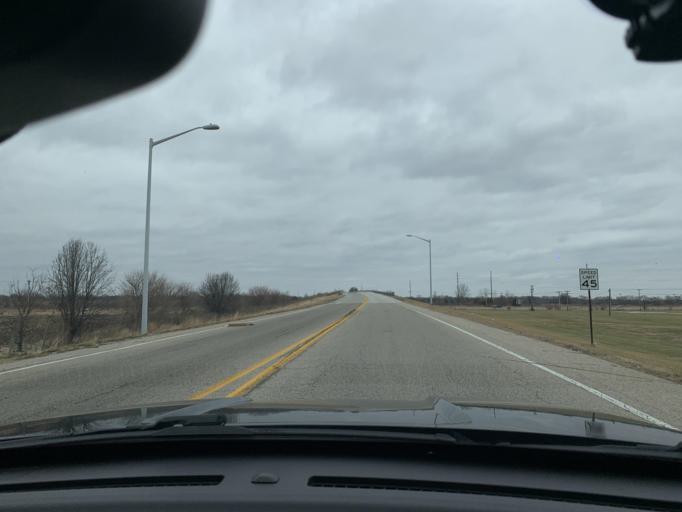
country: US
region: Illinois
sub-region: Sangamon County
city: Jerome
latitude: 39.7397
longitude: -89.6883
